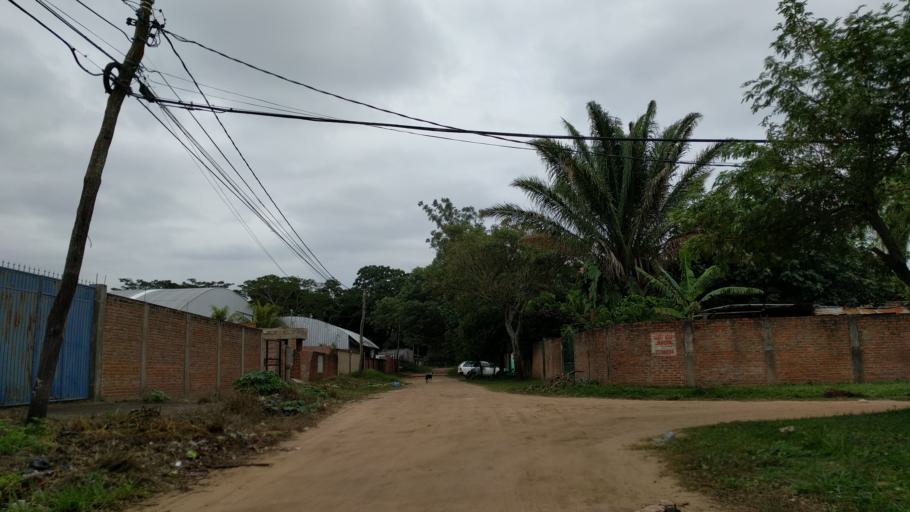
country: BO
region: Santa Cruz
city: Santa Cruz de la Sierra
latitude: -17.8079
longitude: -63.2208
